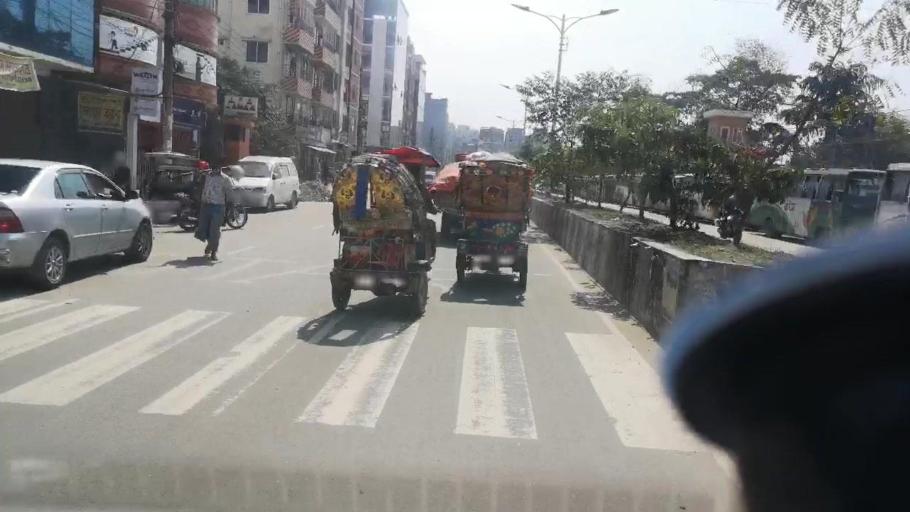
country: BD
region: Dhaka
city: Tungi
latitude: 23.8731
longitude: 90.3796
